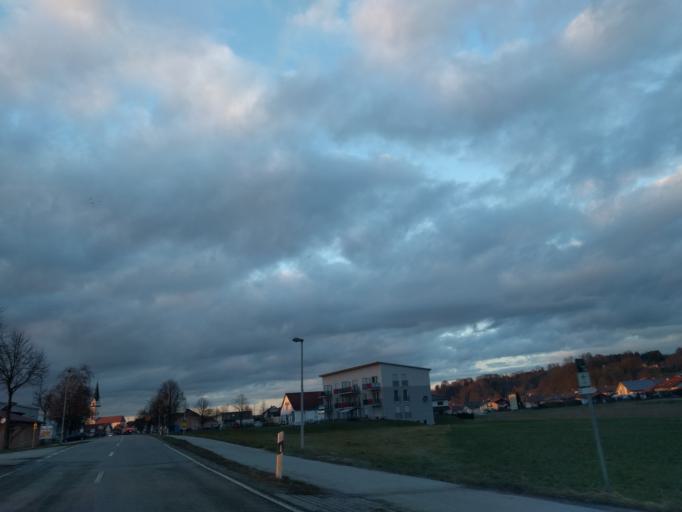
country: DE
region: Bavaria
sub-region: Lower Bavaria
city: Hofkirchen
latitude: 48.6732
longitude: 13.1227
